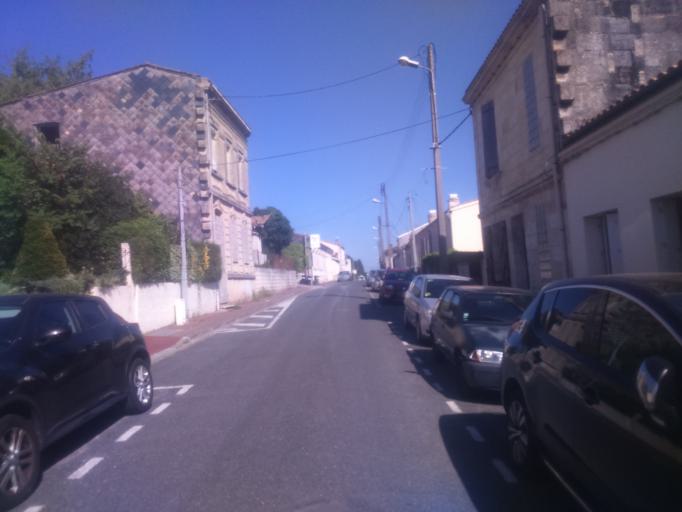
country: FR
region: Aquitaine
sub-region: Departement de la Gironde
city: Lormont
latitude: 44.8773
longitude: -0.5247
